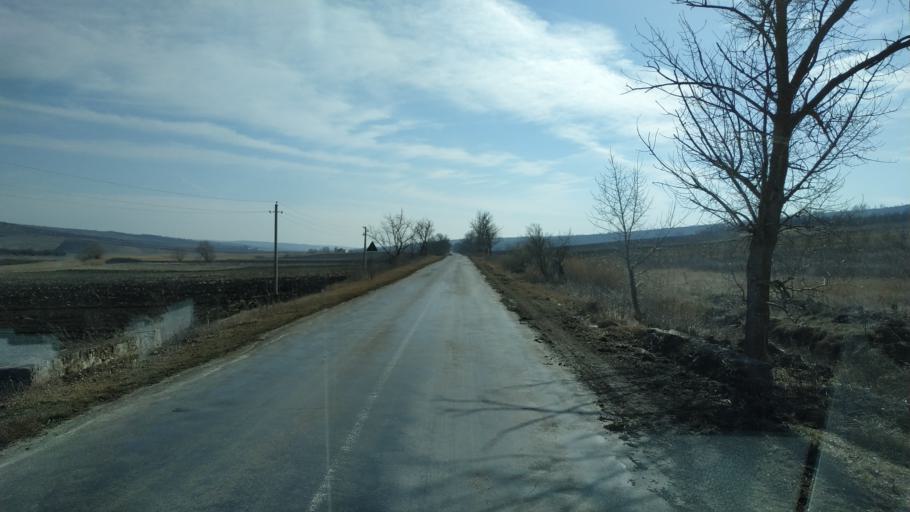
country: MD
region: Nisporeni
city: Nisporeni
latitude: 47.1179
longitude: 28.1220
